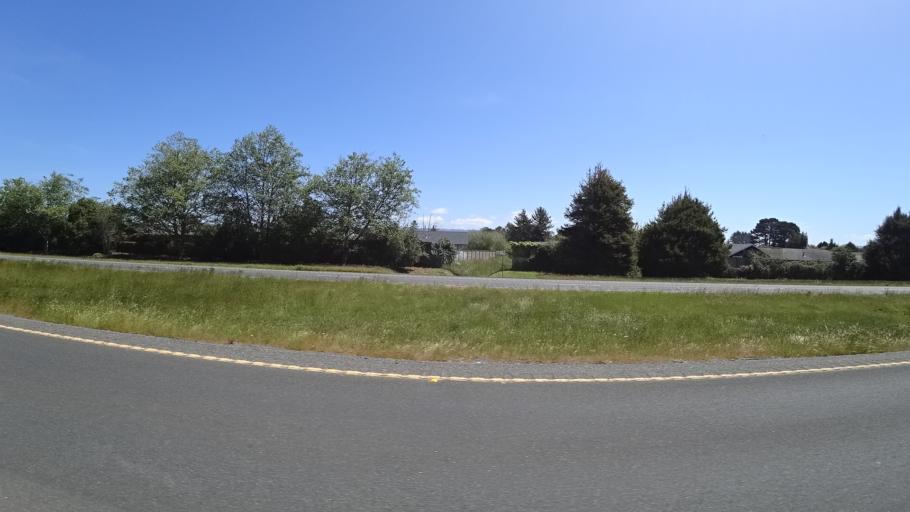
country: US
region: California
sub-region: Humboldt County
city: McKinleyville
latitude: 40.9465
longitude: -124.1164
